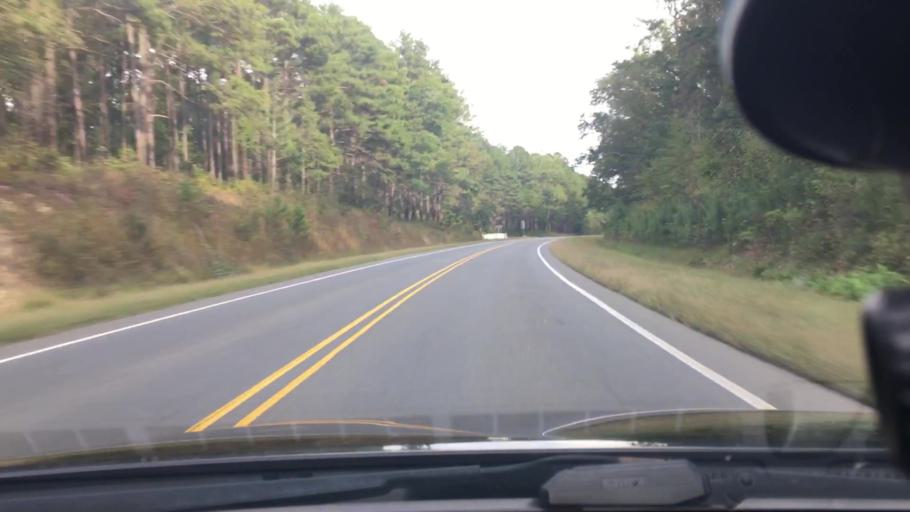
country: US
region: North Carolina
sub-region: Montgomery County
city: Troy
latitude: 35.3226
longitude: -79.9559
